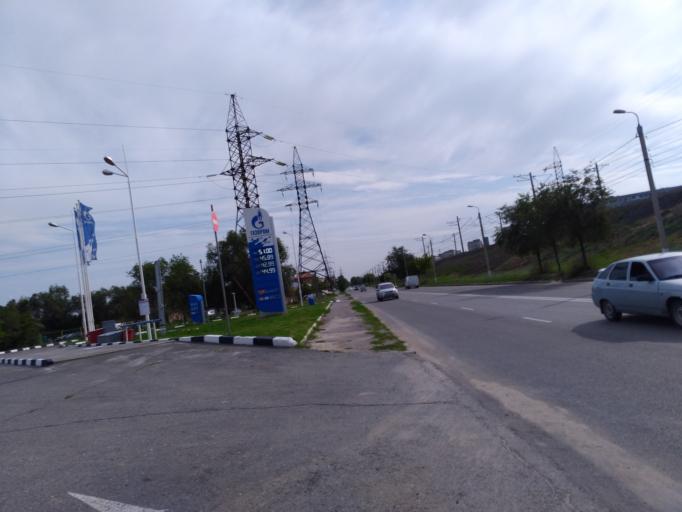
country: RU
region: Volgograd
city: Volgograd
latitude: 48.7063
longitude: 44.4959
